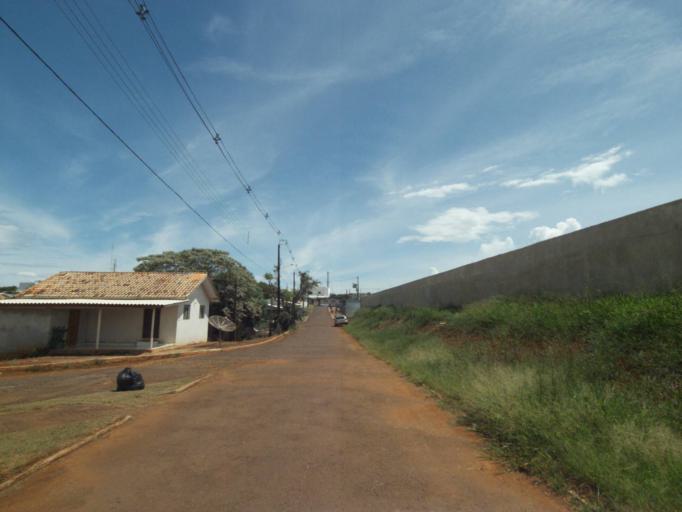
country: BR
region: Parana
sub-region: Guaraniacu
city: Guaraniacu
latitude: -25.0970
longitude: -52.8668
